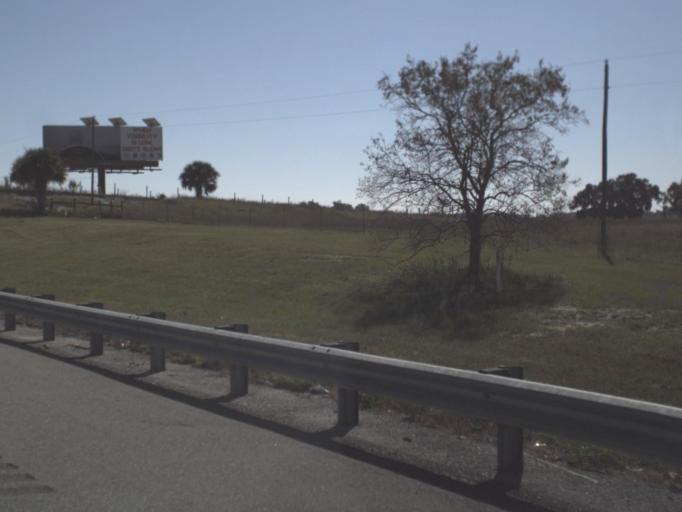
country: US
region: Florida
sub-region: Lake County
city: Leesburg
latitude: 28.7817
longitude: -81.9734
